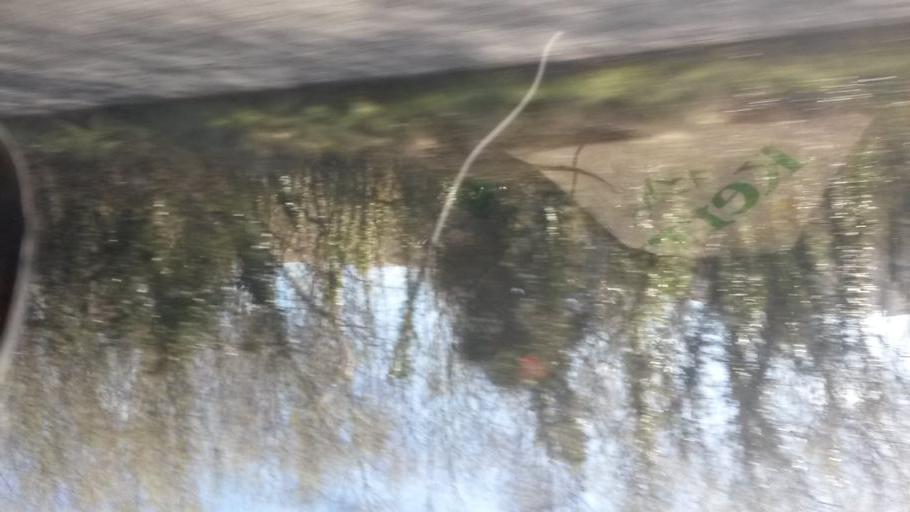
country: IE
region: Munster
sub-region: Ciarrai
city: Cill Airne
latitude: 51.9152
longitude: -9.3941
